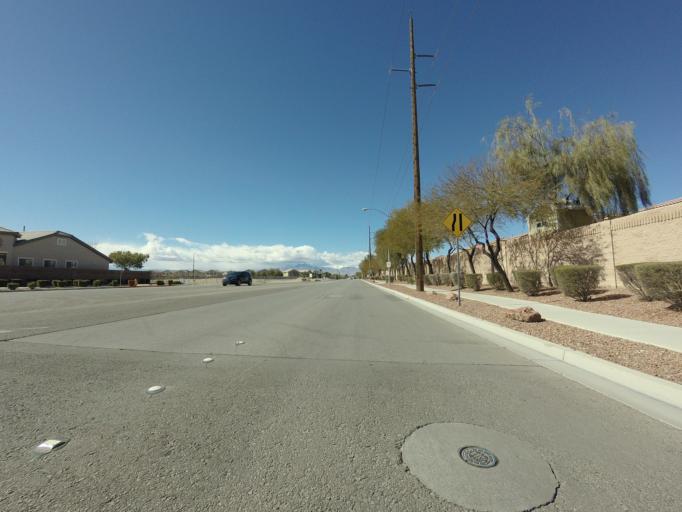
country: US
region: Nevada
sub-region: Clark County
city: Nellis Air Force Base
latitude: 36.2692
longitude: -115.0963
